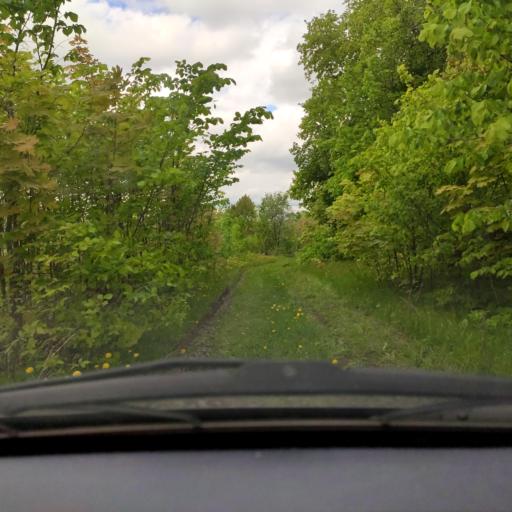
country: RU
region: Bashkortostan
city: Kabakovo
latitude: 54.7113
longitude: 56.1589
